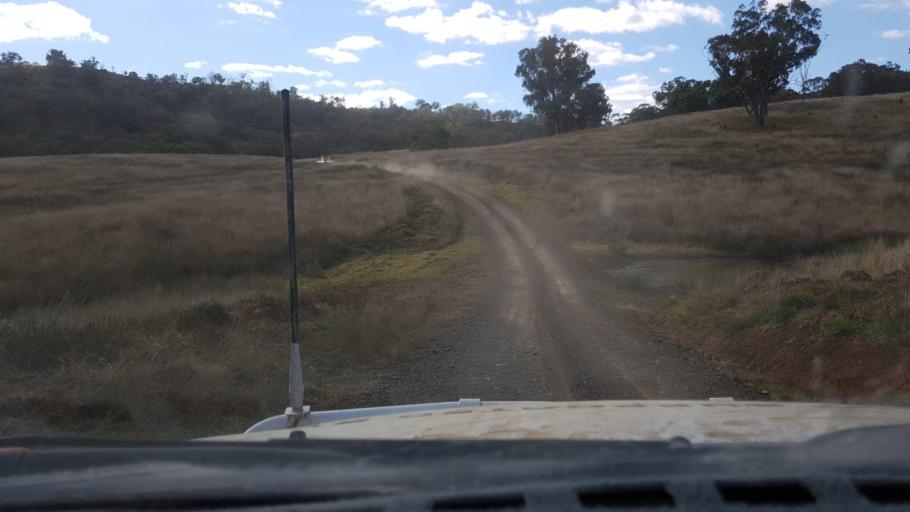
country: AU
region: New South Wales
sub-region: Tamworth Municipality
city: Manilla
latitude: -30.4327
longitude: 150.7920
